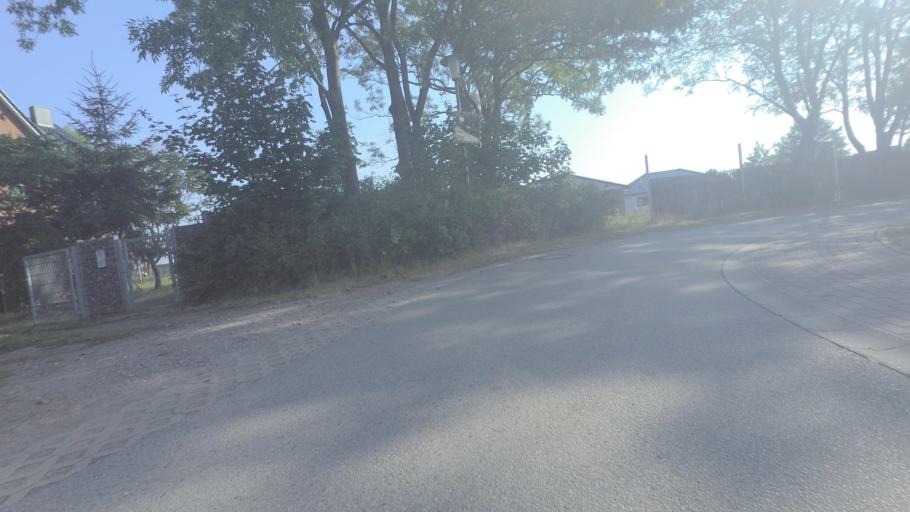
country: DE
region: Mecklenburg-Vorpommern
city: Grimmen
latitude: 54.1281
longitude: 13.0450
